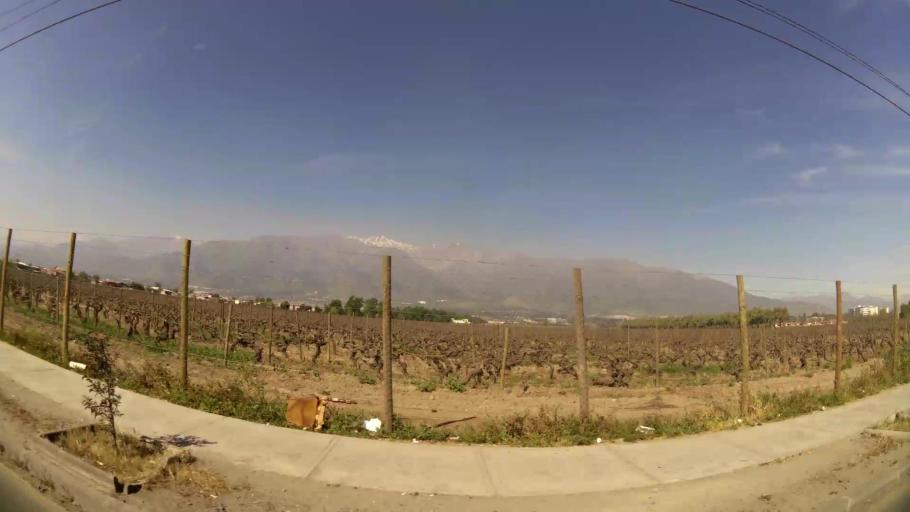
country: CL
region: Santiago Metropolitan
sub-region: Provincia de Santiago
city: Villa Presidente Frei, Nunoa, Santiago, Chile
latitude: -33.4819
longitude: -70.5788
